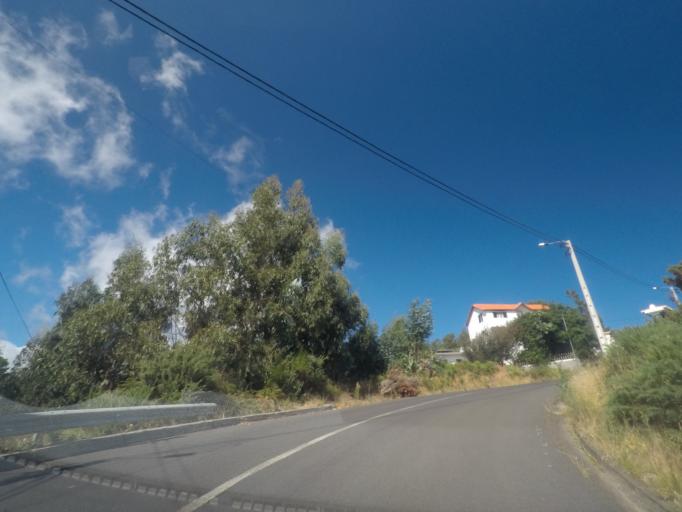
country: PT
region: Madeira
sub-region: Ribeira Brava
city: Campanario
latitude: 32.6944
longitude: -17.0331
